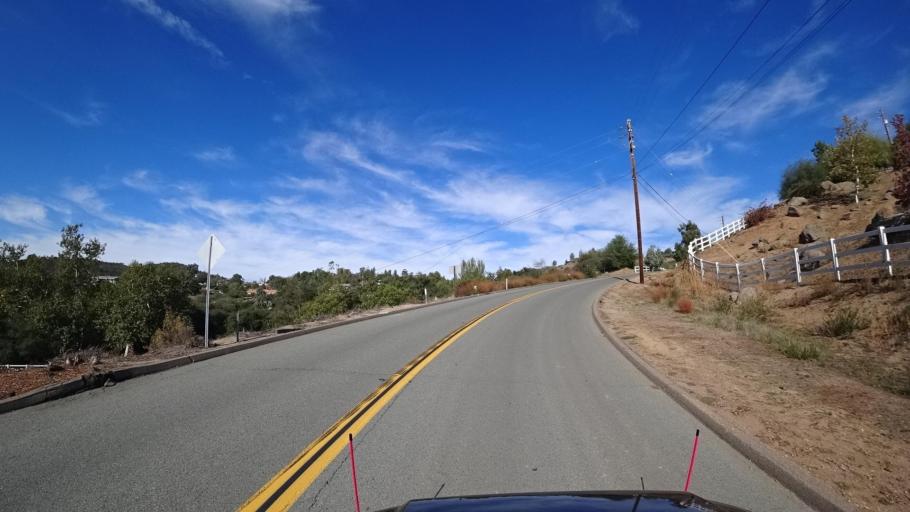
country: US
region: California
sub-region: San Diego County
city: Alpine
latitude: 32.8155
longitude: -116.7413
